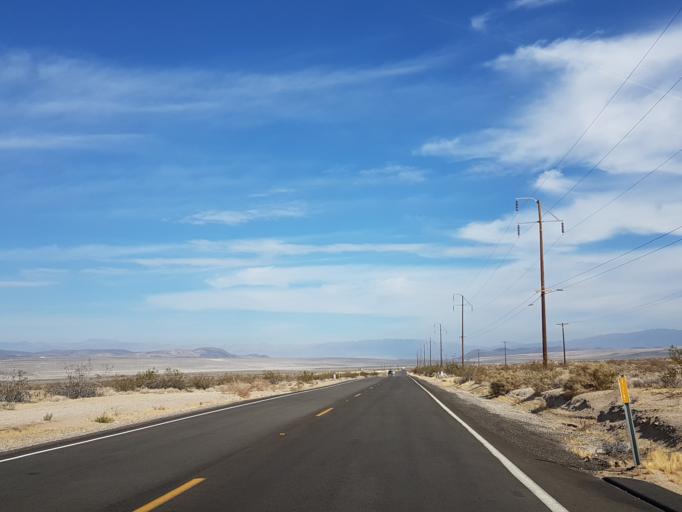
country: US
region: California
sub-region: Kern County
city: Ridgecrest
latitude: 35.6415
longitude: -117.5518
